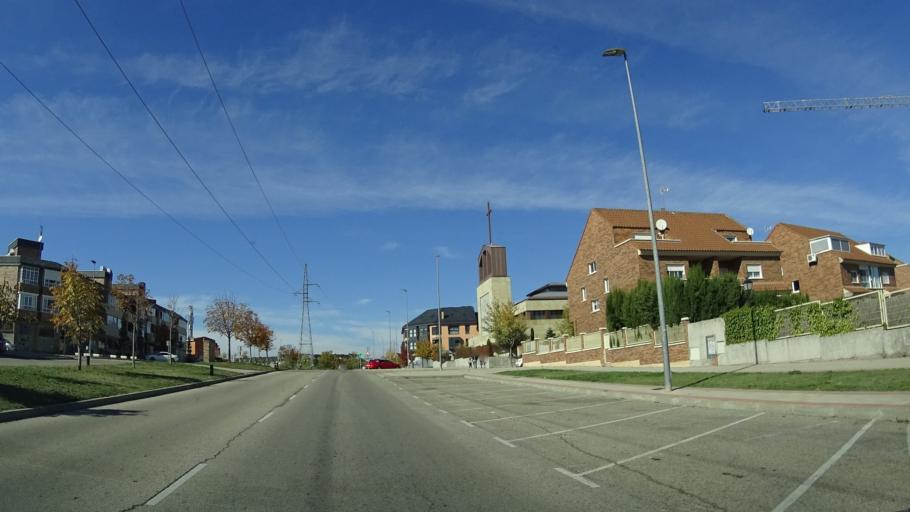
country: ES
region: Madrid
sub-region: Provincia de Madrid
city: Villanueva del Pardillo
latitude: 40.4931
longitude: -3.9596
